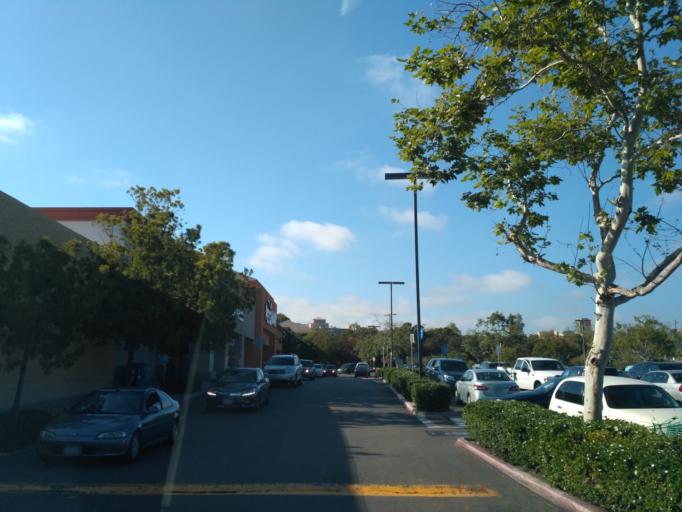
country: US
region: California
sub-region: San Diego County
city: San Diego
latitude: 32.8059
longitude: -117.1158
